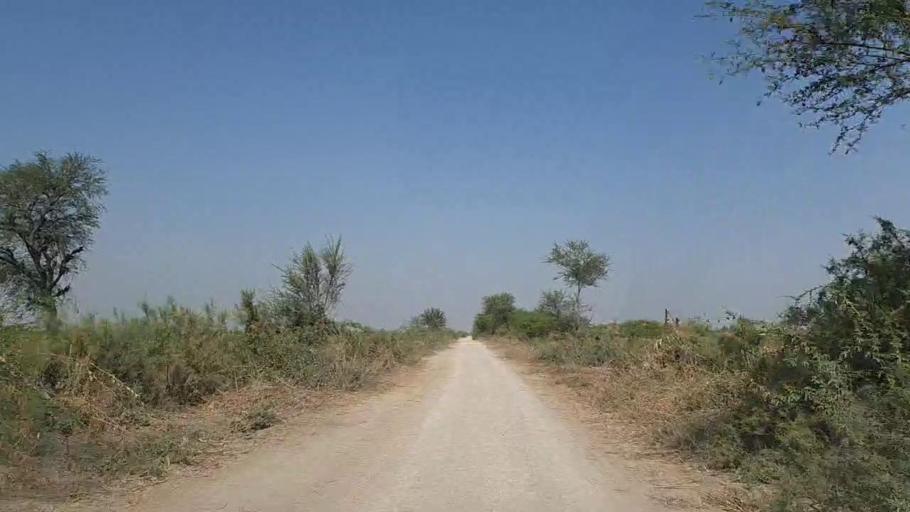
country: PK
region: Sindh
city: Samaro
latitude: 25.1992
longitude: 69.4041
